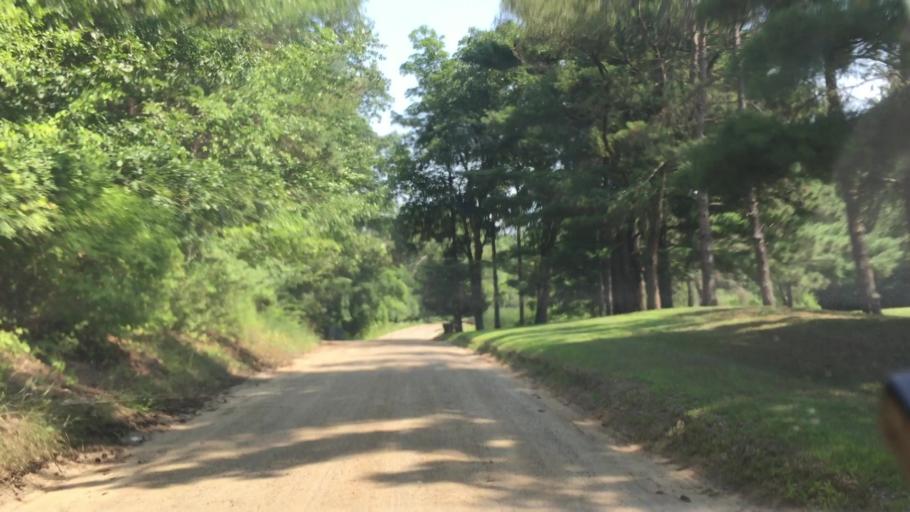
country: US
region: Michigan
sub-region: Oakland County
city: Franklin
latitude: 42.5496
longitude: -83.3333
